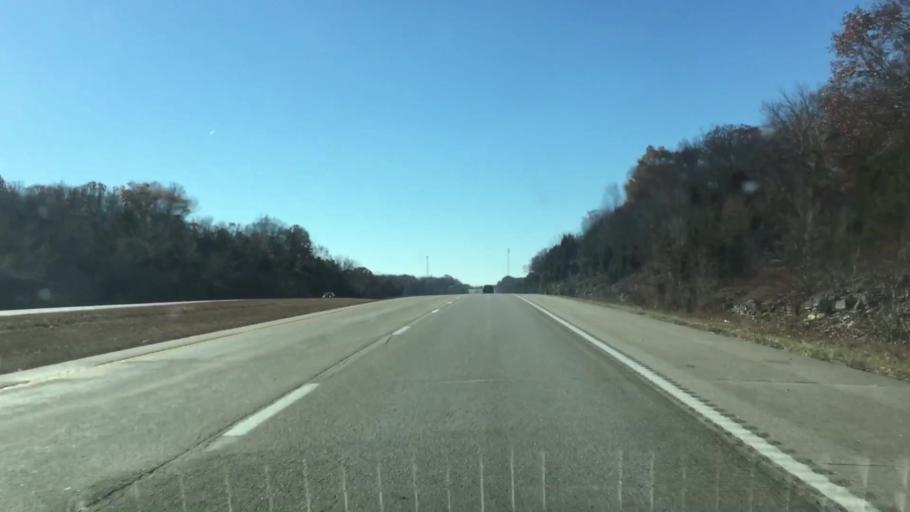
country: US
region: Missouri
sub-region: Cole County
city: Wardsville
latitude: 38.4977
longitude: -92.2682
